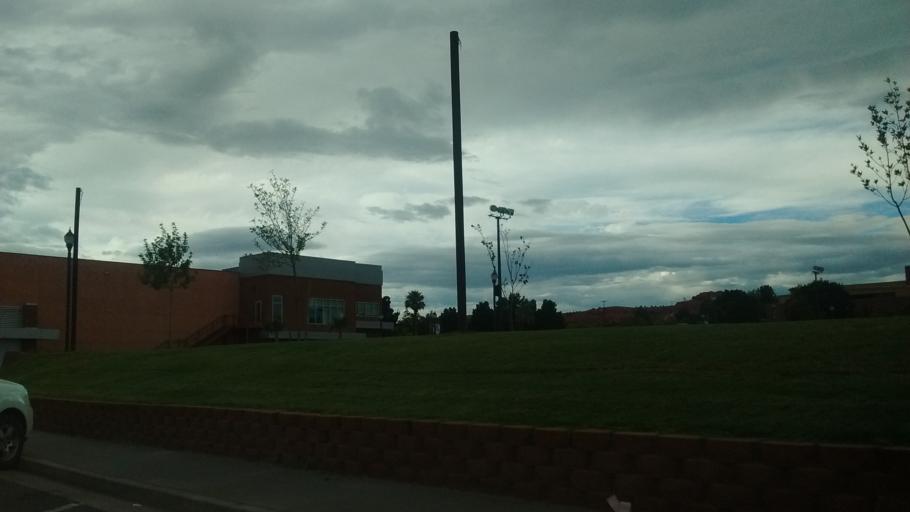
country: US
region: Utah
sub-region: Washington County
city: Saint George
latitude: 37.1014
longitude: -113.5660
